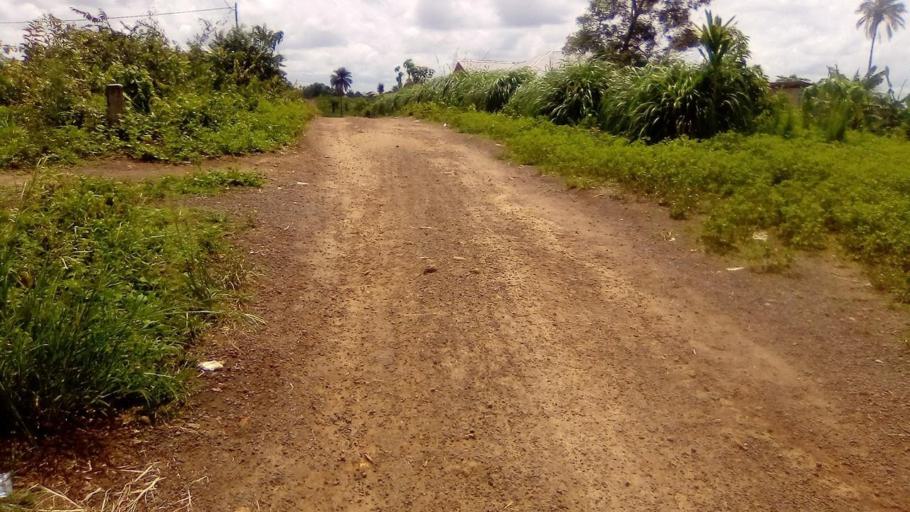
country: SL
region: Southern Province
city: Bo
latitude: 7.9316
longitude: -11.7469
